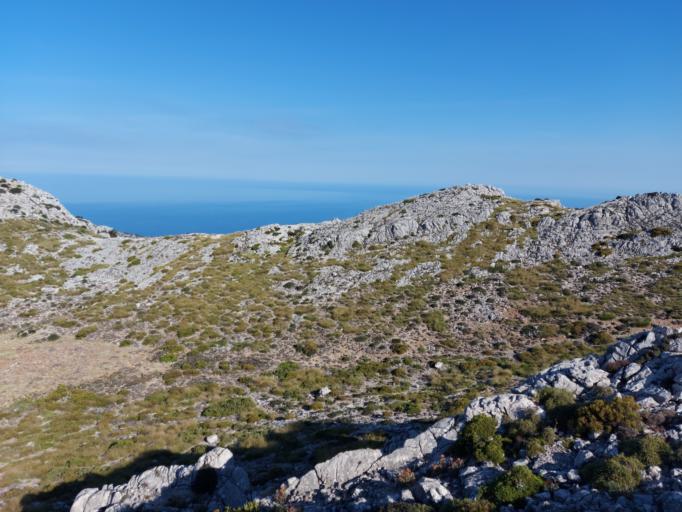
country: ES
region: Balearic Islands
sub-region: Illes Balears
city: Deia
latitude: 39.7315
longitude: 2.6641
